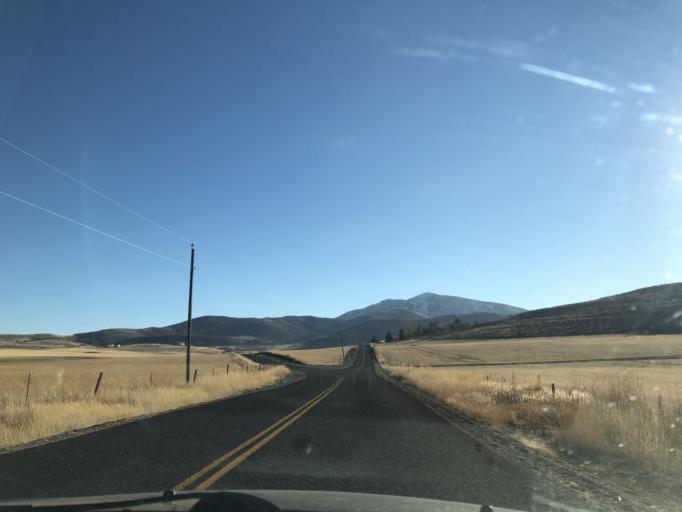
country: US
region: Utah
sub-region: Cache County
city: Wellsville
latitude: 41.6006
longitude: -111.9298
